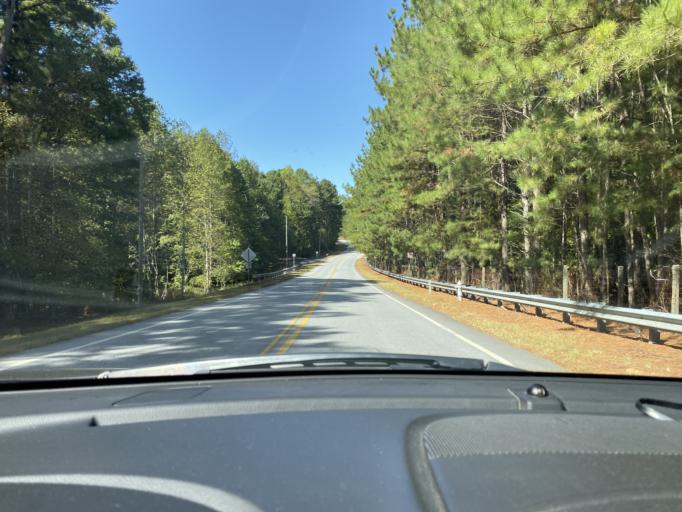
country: US
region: Georgia
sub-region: Gwinnett County
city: Grayson
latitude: 33.9014
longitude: -83.9177
